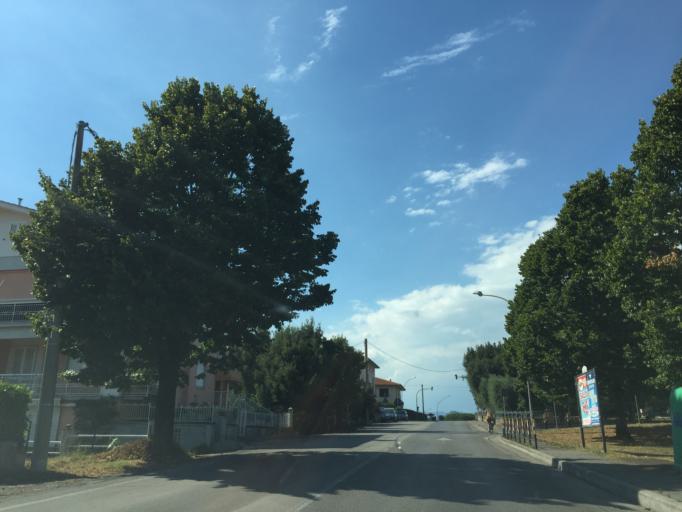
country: IT
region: Tuscany
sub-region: Provincia di Pistoia
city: San Rocco
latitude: 43.8217
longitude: 10.8723
